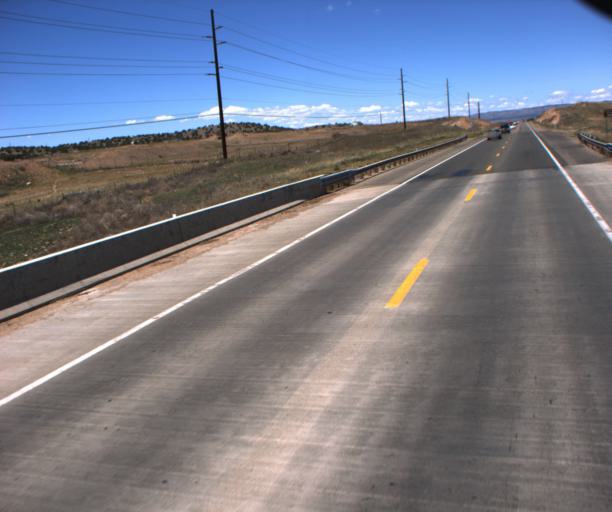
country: US
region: Arizona
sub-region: Yavapai County
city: Paulden
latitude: 34.8298
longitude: -112.4592
